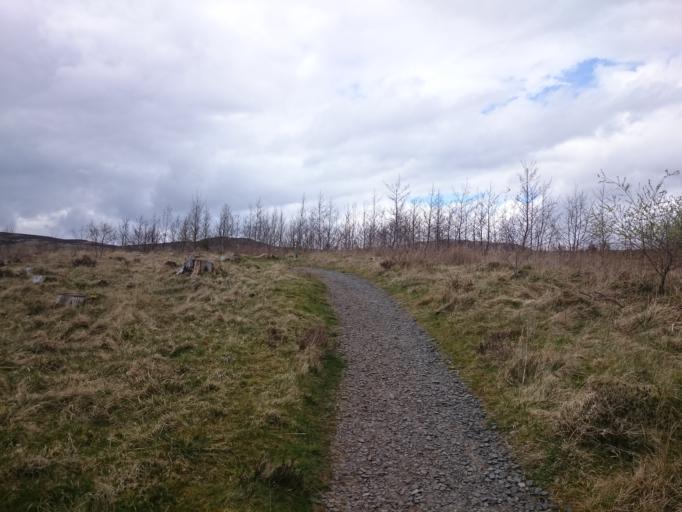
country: GB
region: Scotland
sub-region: Stirling
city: Killearn
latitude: 56.0948
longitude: -4.4888
